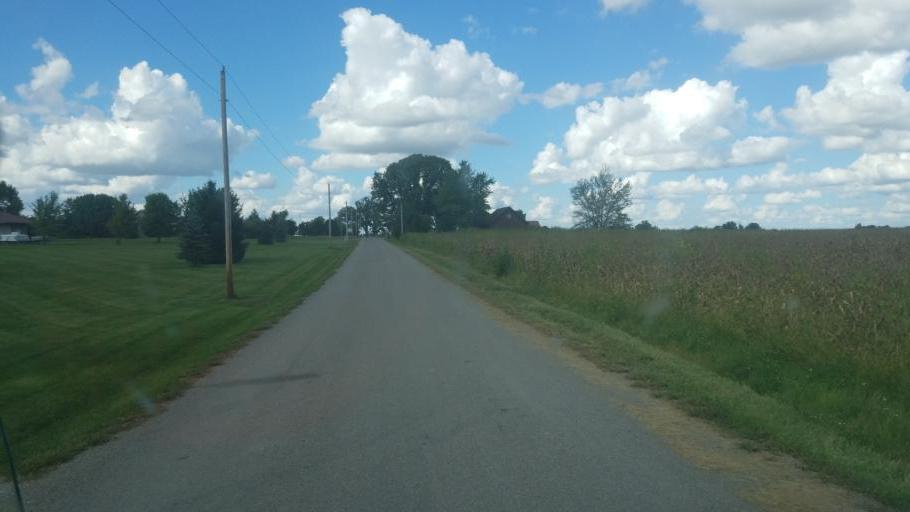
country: US
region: Ohio
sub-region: Hardin County
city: Kenton
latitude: 40.5446
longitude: -83.5444
